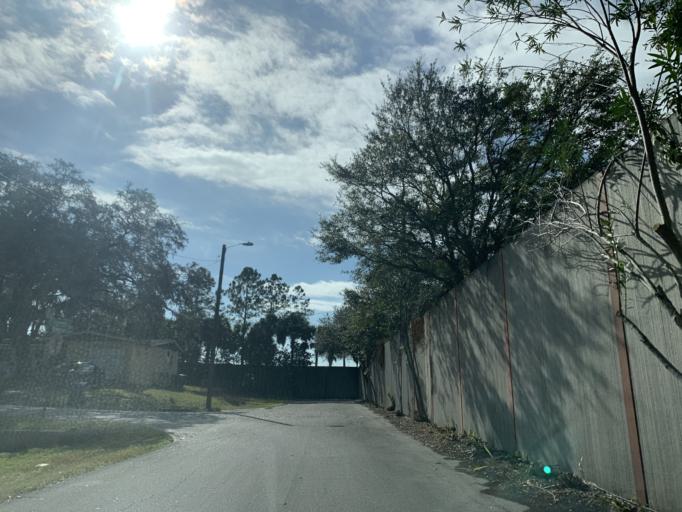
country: US
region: Florida
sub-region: Hillsborough County
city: Temple Terrace
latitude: 28.0372
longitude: -82.4150
